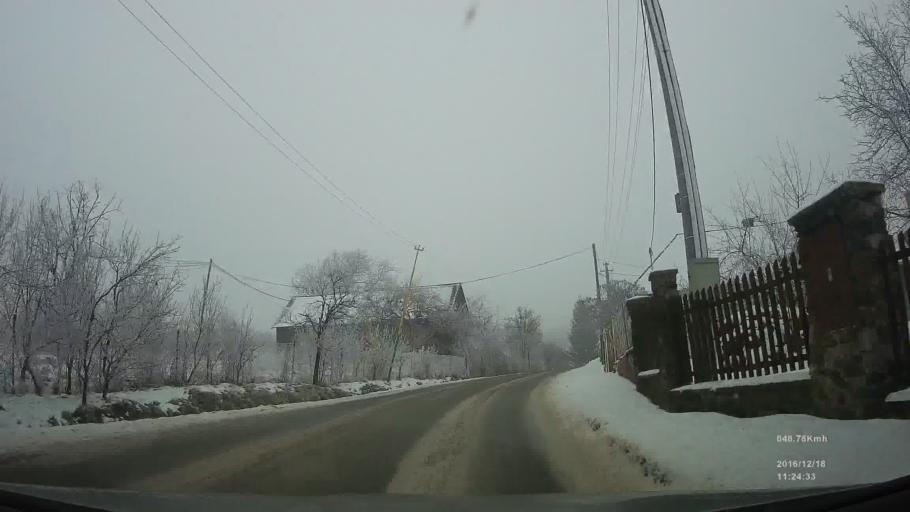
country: SK
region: Presovsky
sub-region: Okres Presov
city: Presov
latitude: 48.8974
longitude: 21.4032
